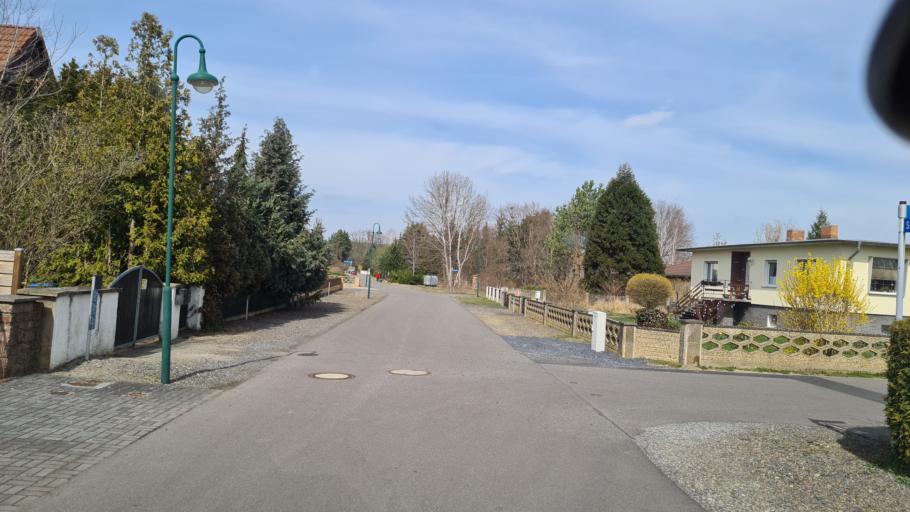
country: DE
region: Brandenburg
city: Lauchhammer
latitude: 51.5107
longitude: 13.7501
